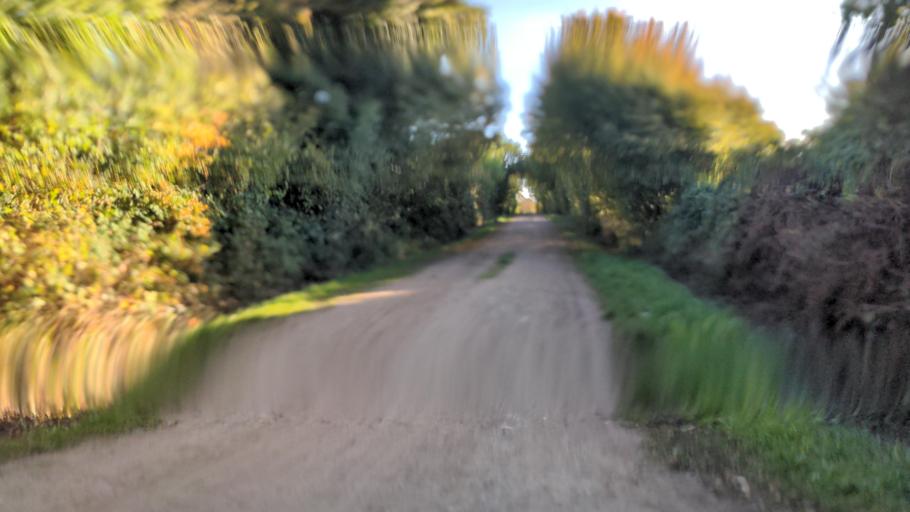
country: DE
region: Schleswig-Holstein
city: Neustadt in Holstein
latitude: 54.0952
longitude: 10.8463
